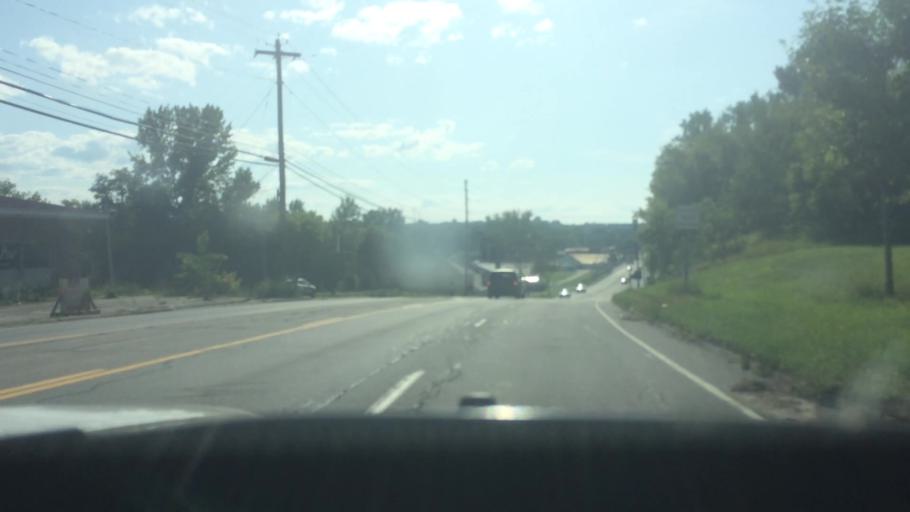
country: US
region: New York
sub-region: Franklin County
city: Malone
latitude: 44.8507
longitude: -74.2740
